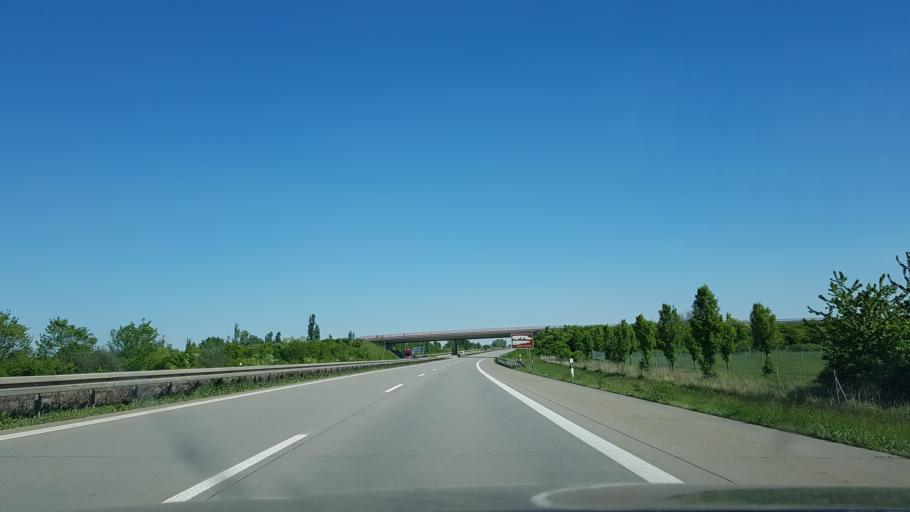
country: DE
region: Saxony
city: Zwenkau
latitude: 51.2612
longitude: 12.2845
